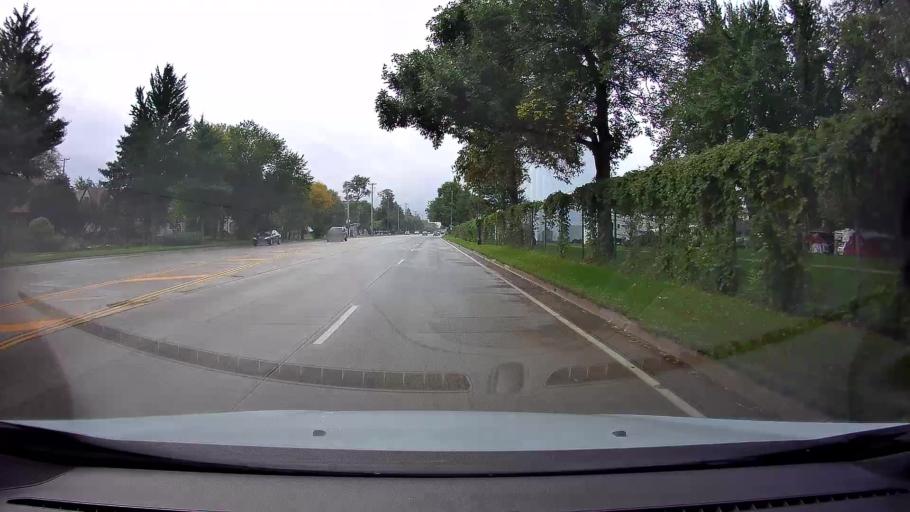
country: US
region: Minnesota
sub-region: Ramsey County
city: Falcon Heights
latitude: 44.9874
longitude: -93.1671
